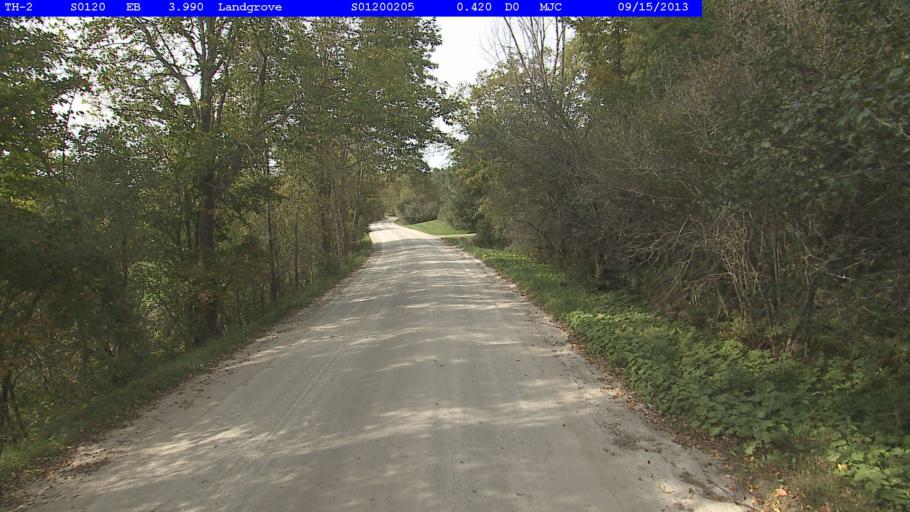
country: US
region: Vermont
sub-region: Bennington County
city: Manchester Center
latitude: 43.2666
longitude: -72.8576
